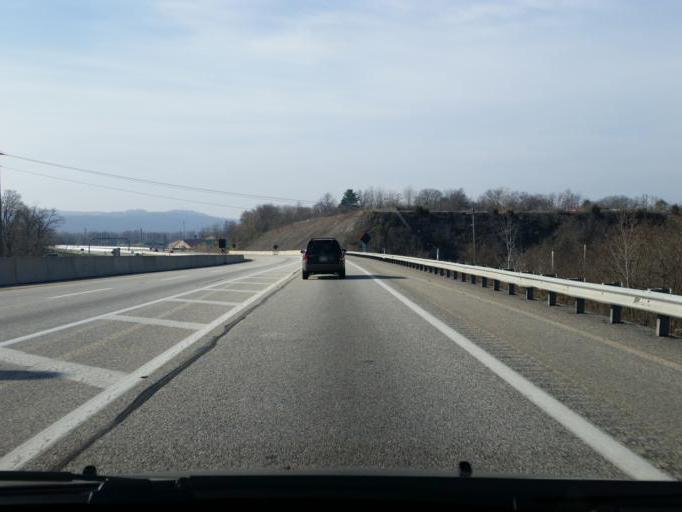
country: US
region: Pennsylvania
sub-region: Dauphin County
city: Highspire
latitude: 40.2144
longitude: -76.7925
